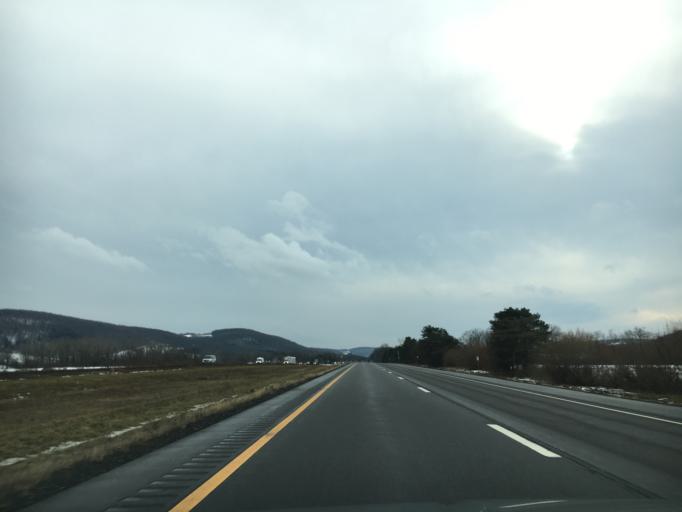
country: US
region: New York
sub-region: Cortland County
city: Homer
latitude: 42.7230
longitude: -76.1454
